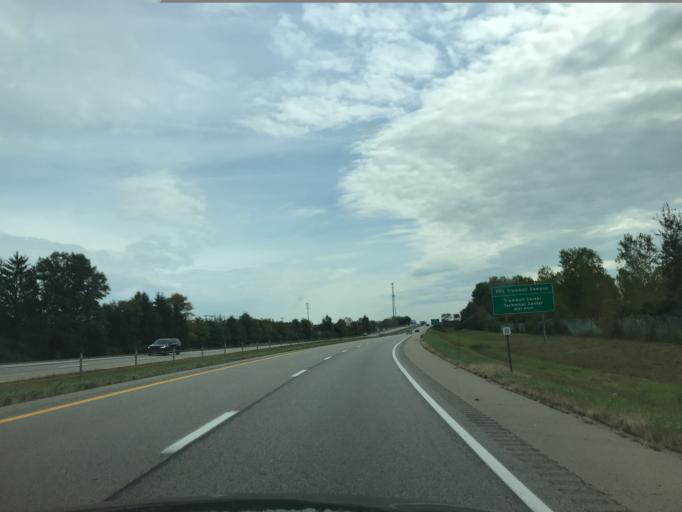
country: US
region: Ohio
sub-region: Trumbull County
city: Champion Heights
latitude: 41.2759
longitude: -80.8574
